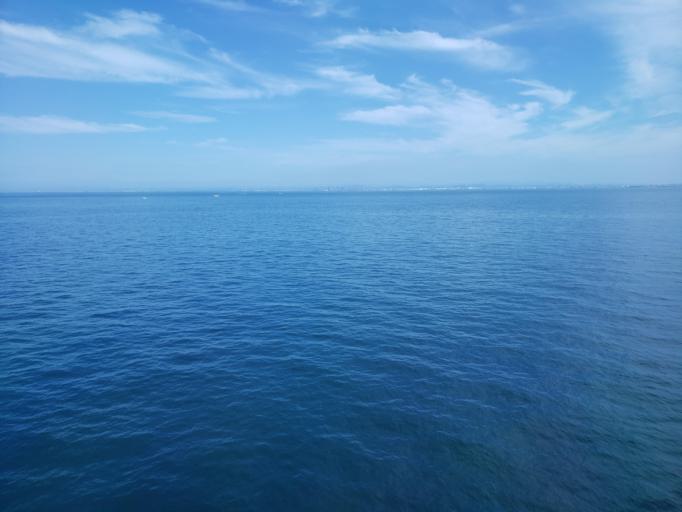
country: JP
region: Hyogo
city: Akashi
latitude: 34.5893
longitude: 134.8832
